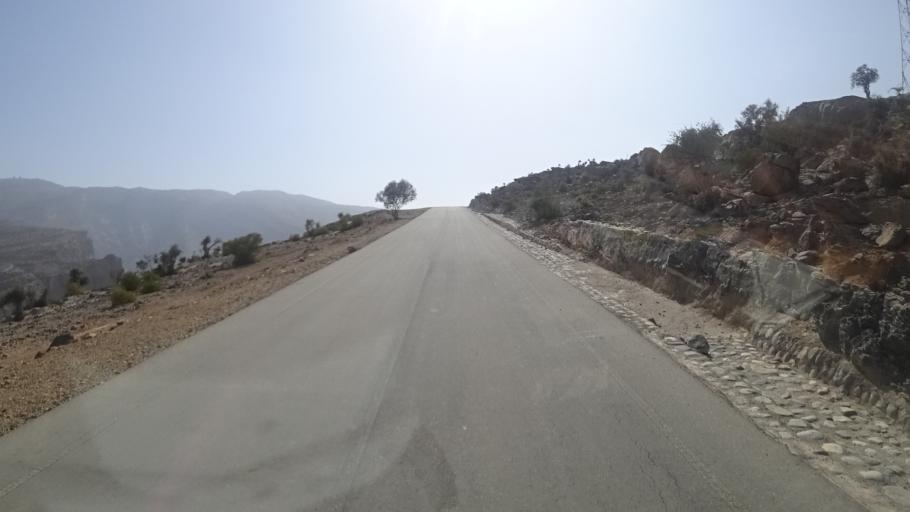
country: OM
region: Muhafazat ad Dakhiliyah
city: Bahla'
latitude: 23.2138
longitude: 57.2023
